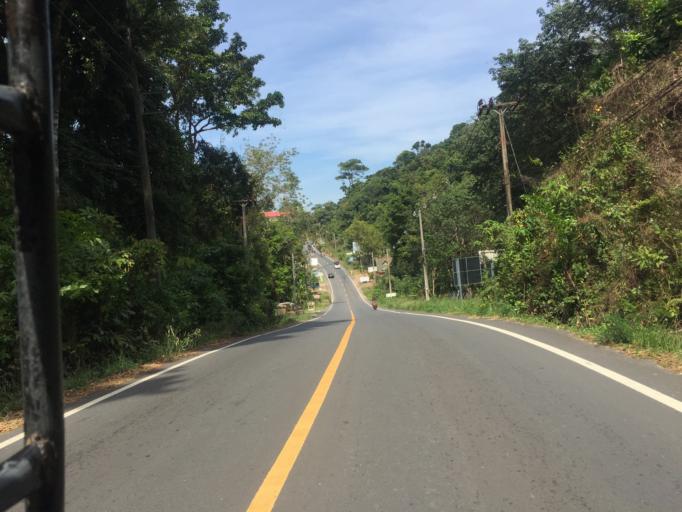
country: TH
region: Trat
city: Laem Ngop
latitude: 12.1374
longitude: 102.2765
